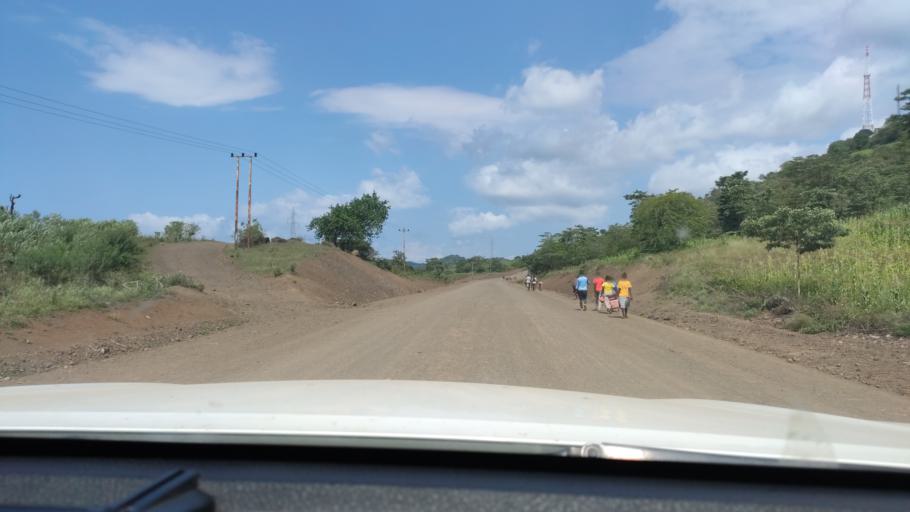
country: ET
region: Southern Nations, Nationalities, and People's Region
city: Felege Neway
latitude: 6.3924
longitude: 37.0703
